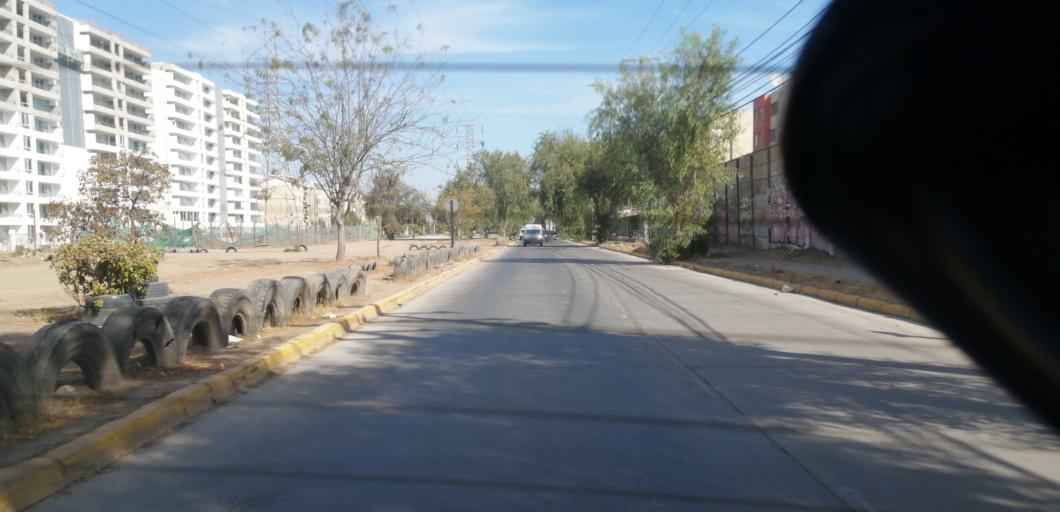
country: CL
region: Santiago Metropolitan
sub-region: Provincia de Santiago
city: Lo Prado
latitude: -33.4572
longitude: -70.7314
